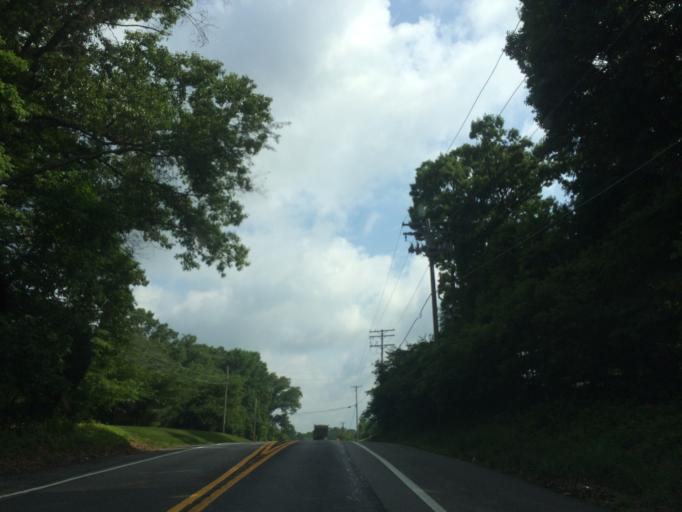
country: US
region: Maryland
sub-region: Carroll County
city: Sykesville
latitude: 39.2731
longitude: -77.0361
